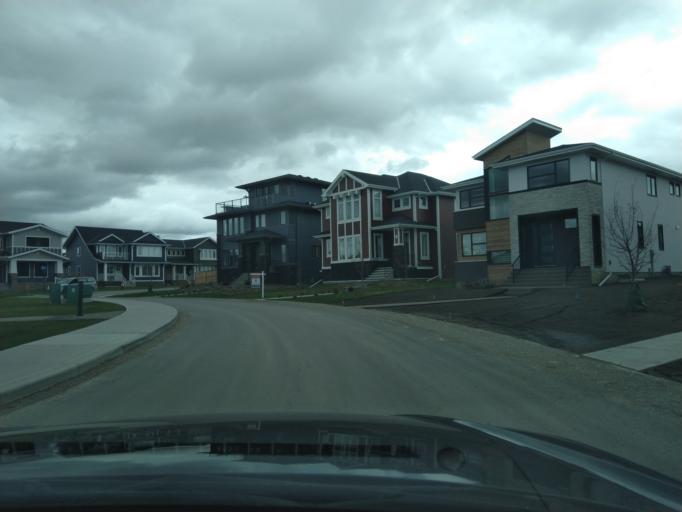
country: CA
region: Alberta
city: Cochrane
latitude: 51.1111
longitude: -114.3952
